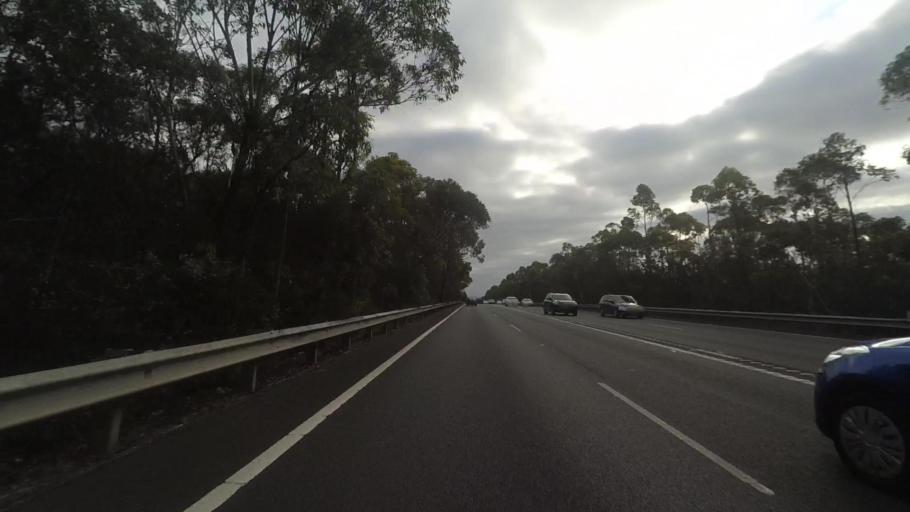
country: AU
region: New South Wales
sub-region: Sutherland Shire
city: Menai
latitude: -34.0003
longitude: 151.0224
